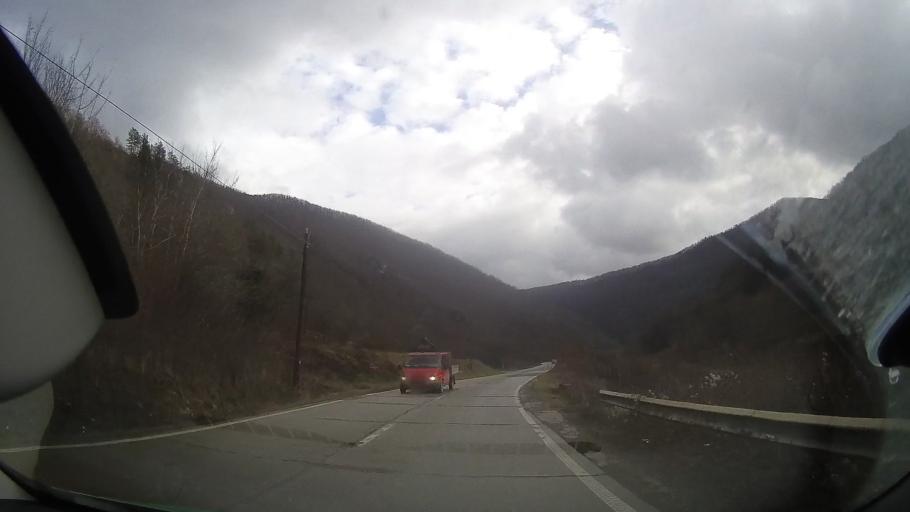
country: RO
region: Alba
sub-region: Comuna Rimetea
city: Rimetea
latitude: 46.5102
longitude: 23.5660
